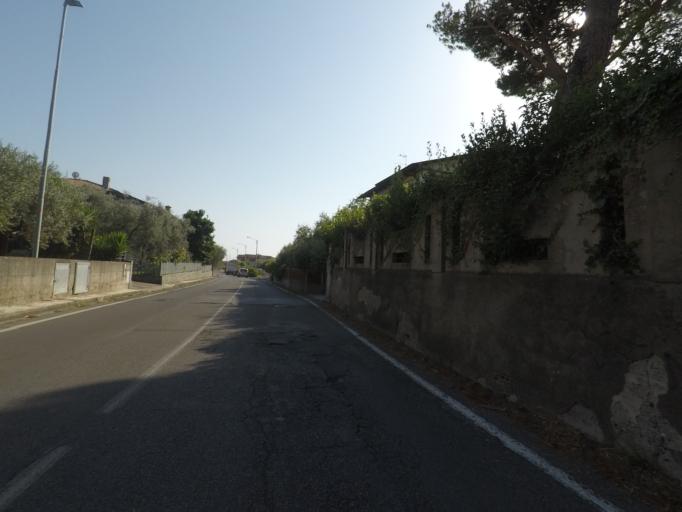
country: IT
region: Liguria
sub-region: Provincia di La Spezia
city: Casano-Dogana-Isola
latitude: 44.0742
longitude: 10.0270
